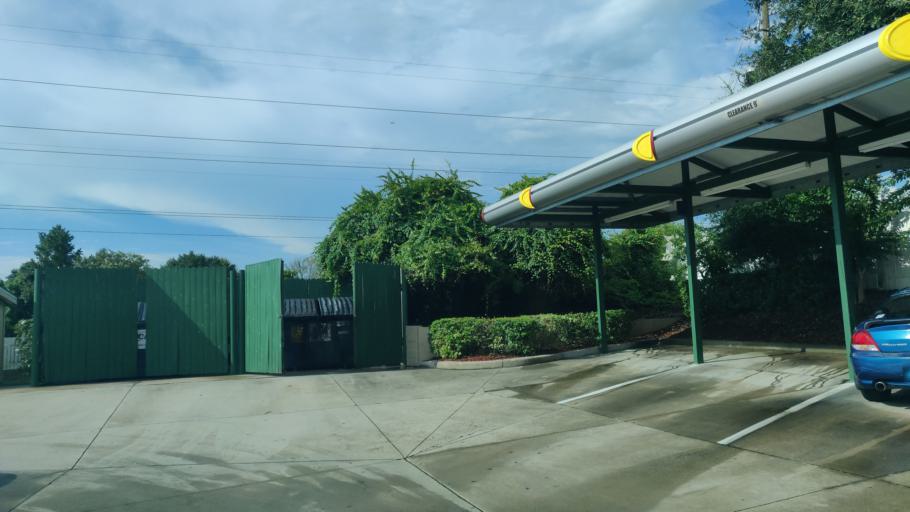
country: US
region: Florida
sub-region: Volusia County
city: Deltona
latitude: 28.9117
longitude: -81.2778
